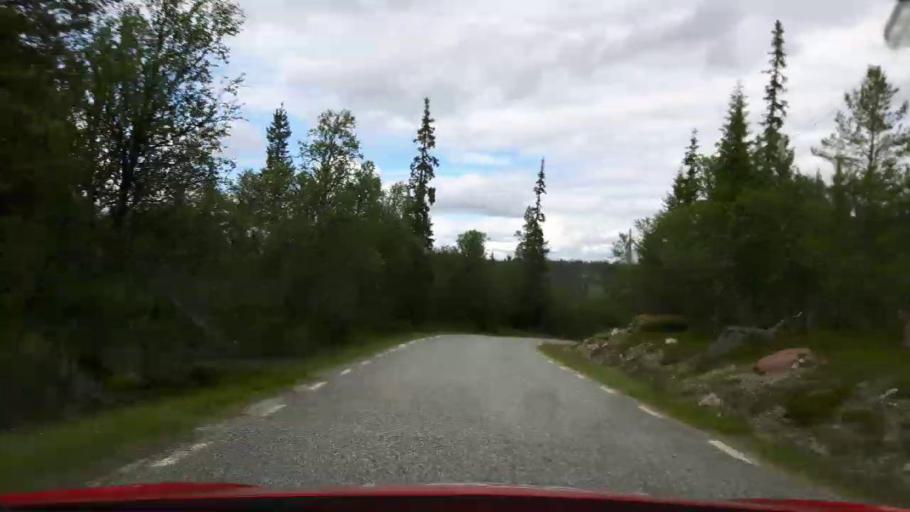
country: NO
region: Hedmark
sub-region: Engerdal
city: Engerdal
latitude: 62.3535
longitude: 12.7935
